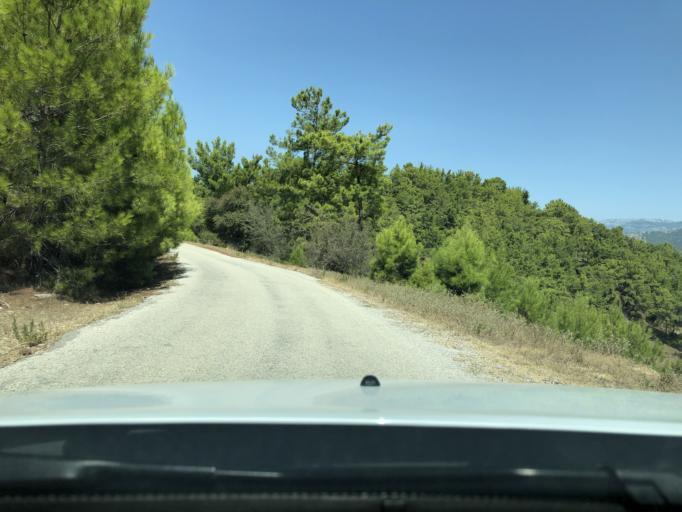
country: TR
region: Antalya
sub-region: Manavgat
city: Manavgat
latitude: 36.8378
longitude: 31.5341
